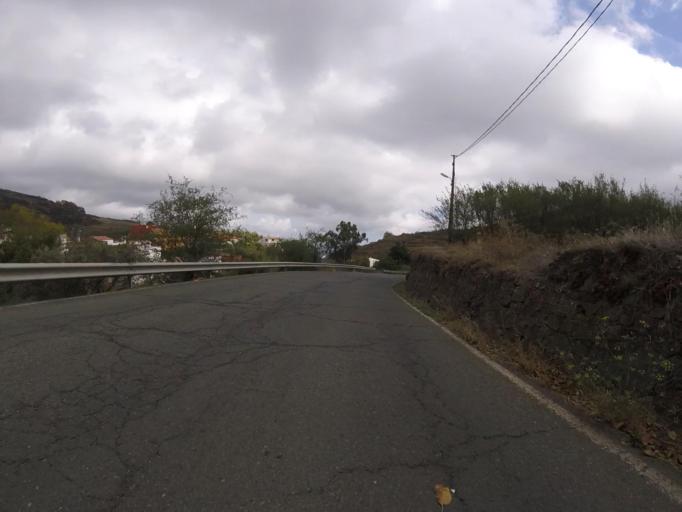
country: ES
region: Canary Islands
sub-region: Provincia de Las Palmas
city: Vega de San Mateo
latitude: 27.9908
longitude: -15.5684
